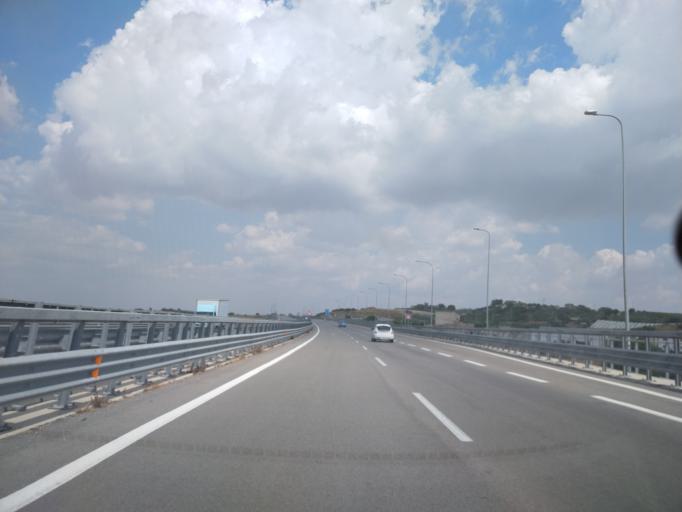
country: IT
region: Sicily
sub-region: Agrigento
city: Canicatti
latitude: 37.3805
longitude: 13.8054
